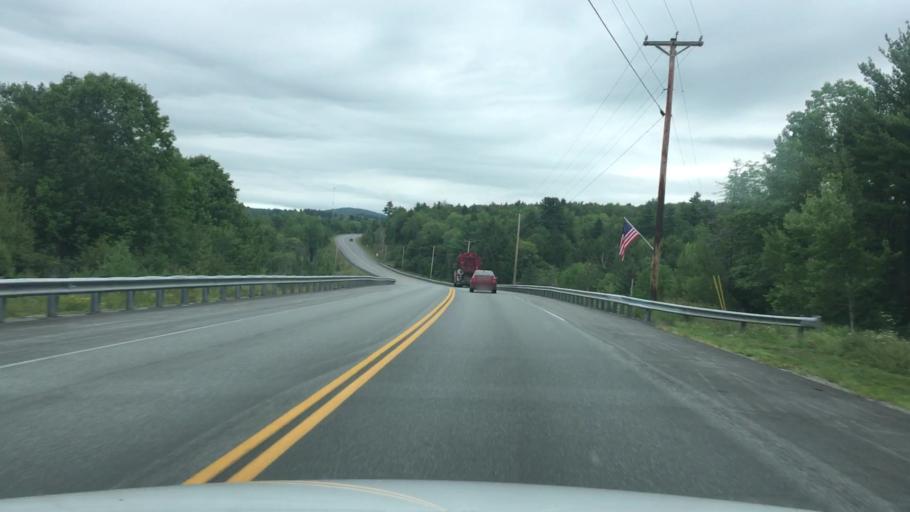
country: US
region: Maine
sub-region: Hancock County
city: Franklin
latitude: 44.8398
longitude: -68.3465
